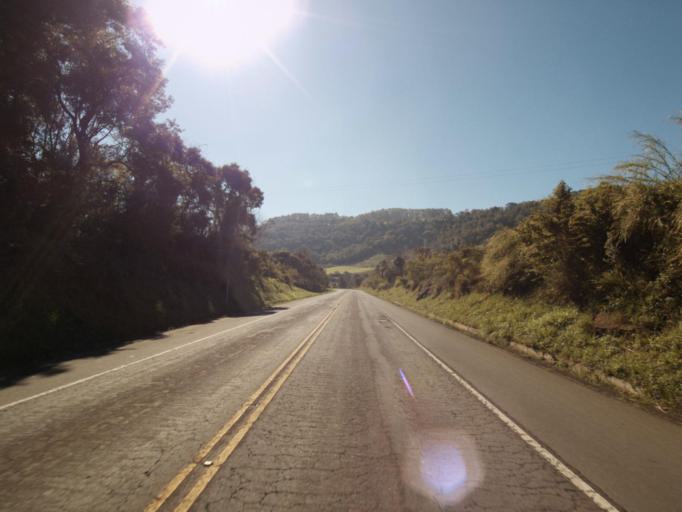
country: BR
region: Rio Grande do Sul
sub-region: Frederico Westphalen
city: Frederico Westphalen
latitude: -26.9938
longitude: -53.2277
